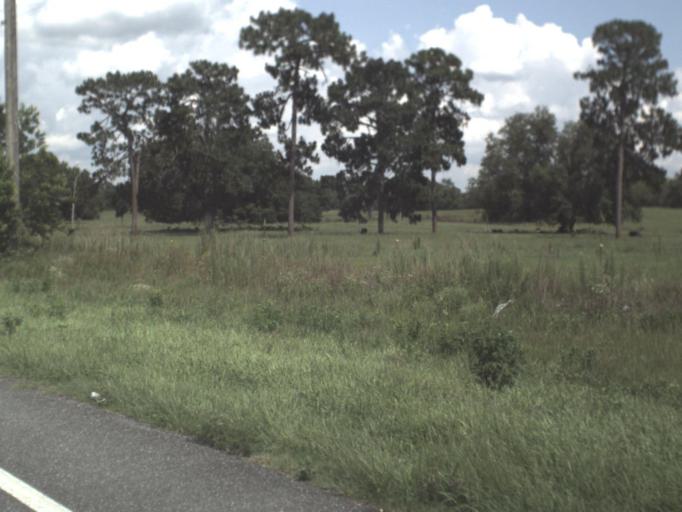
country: US
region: Florida
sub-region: Alachua County
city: Newberry
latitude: 29.6330
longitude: -82.6969
